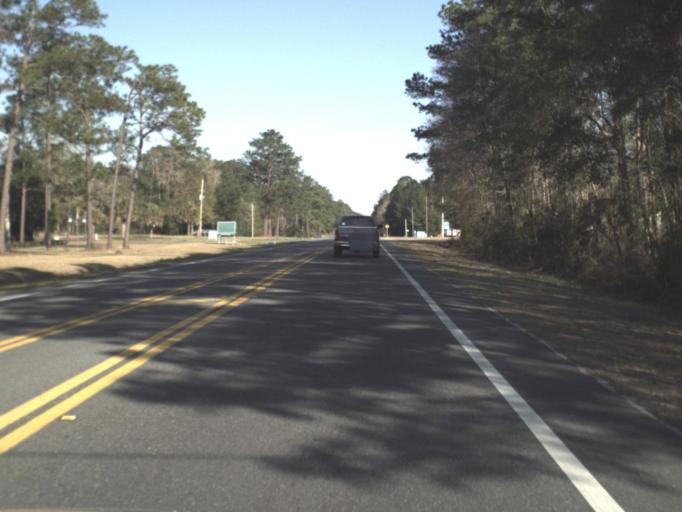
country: US
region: Florida
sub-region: Jackson County
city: Marianna
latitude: 30.7467
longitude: -85.1780
